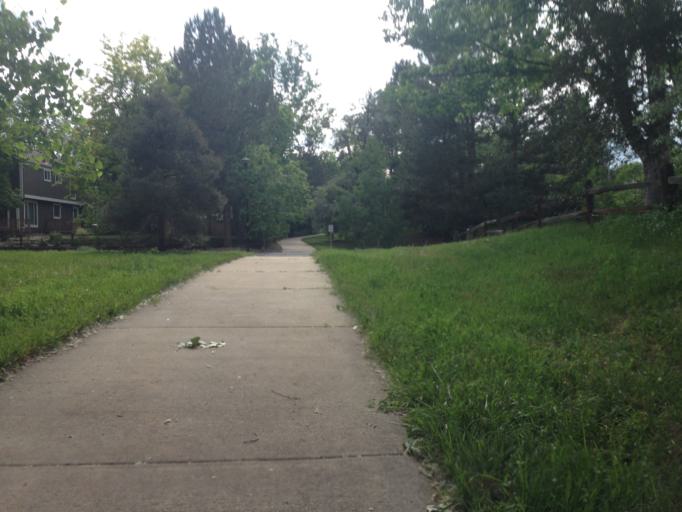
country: US
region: Colorado
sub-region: Boulder County
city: Louisville
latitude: 39.9760
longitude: -105.1468
